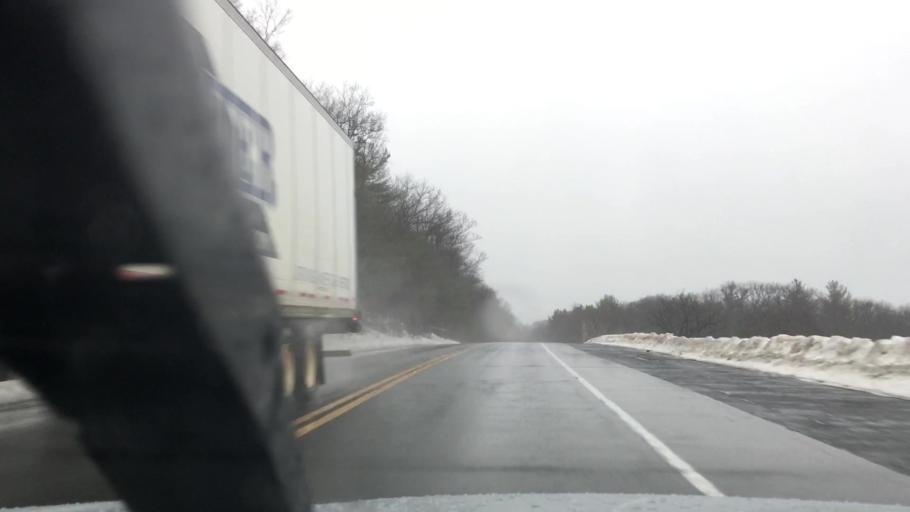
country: US
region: Massachusetts
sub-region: Hampshire County
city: Pelham
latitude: 42.4007
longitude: -72.4042
